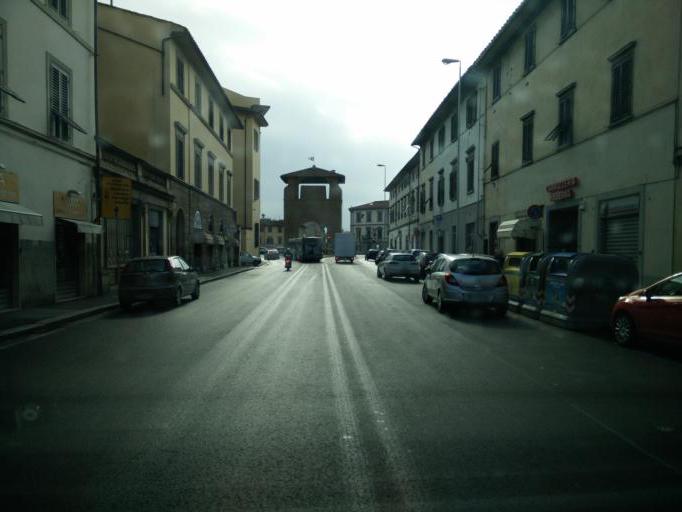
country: IT
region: Tuscany
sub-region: Province of Florence
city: Florence
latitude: 43.7788
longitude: 11.2390
